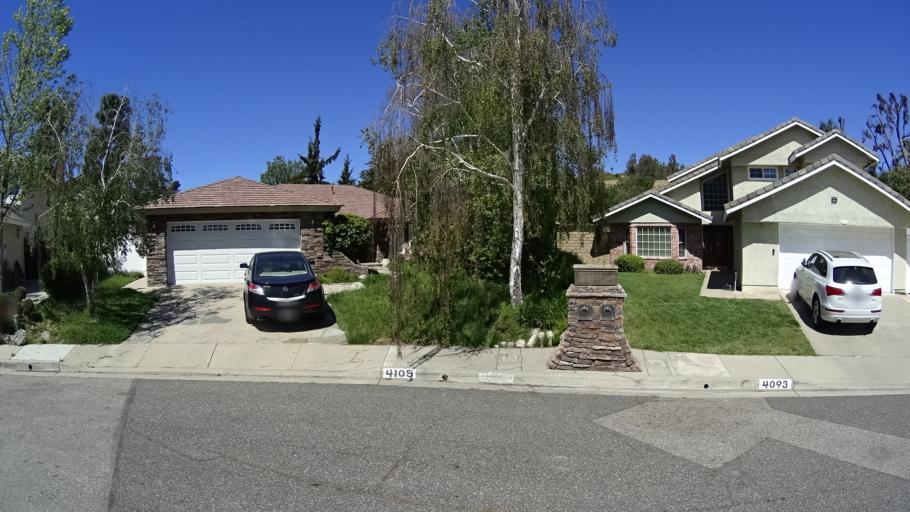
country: US
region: California
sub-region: Ventura County
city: Casa Conejo
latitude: 34.1602
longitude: -118.9624
